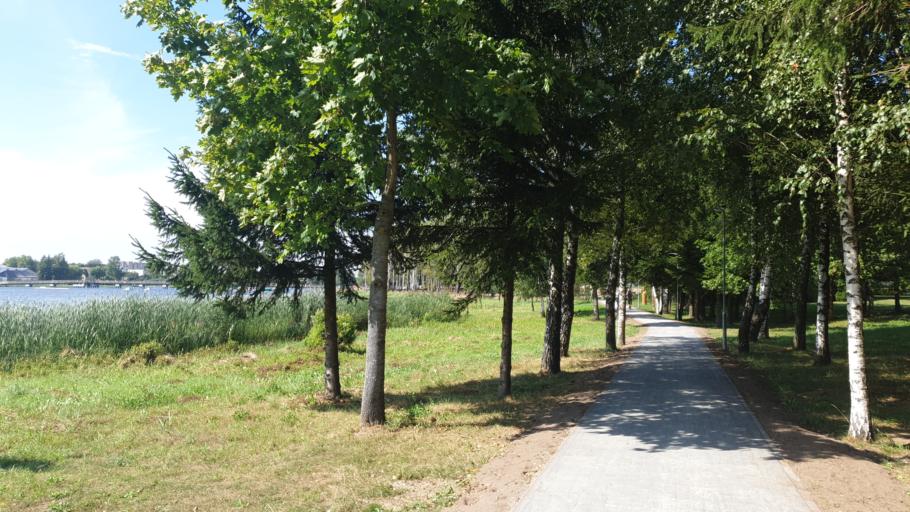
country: LT
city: Sirvintos
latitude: 55.0409
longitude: 24.9645
